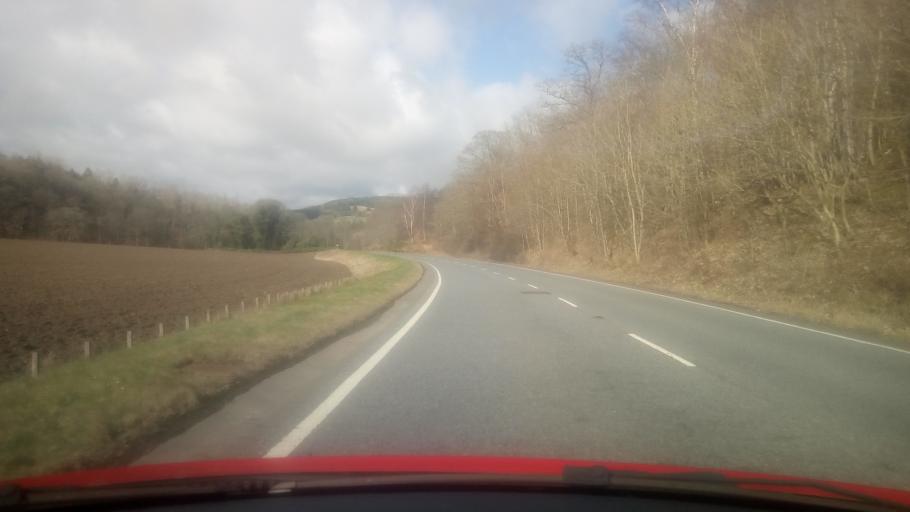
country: GB
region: Scotland
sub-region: The Scottish Borders
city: Selkirk
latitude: 55.6149
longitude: -2.9164
